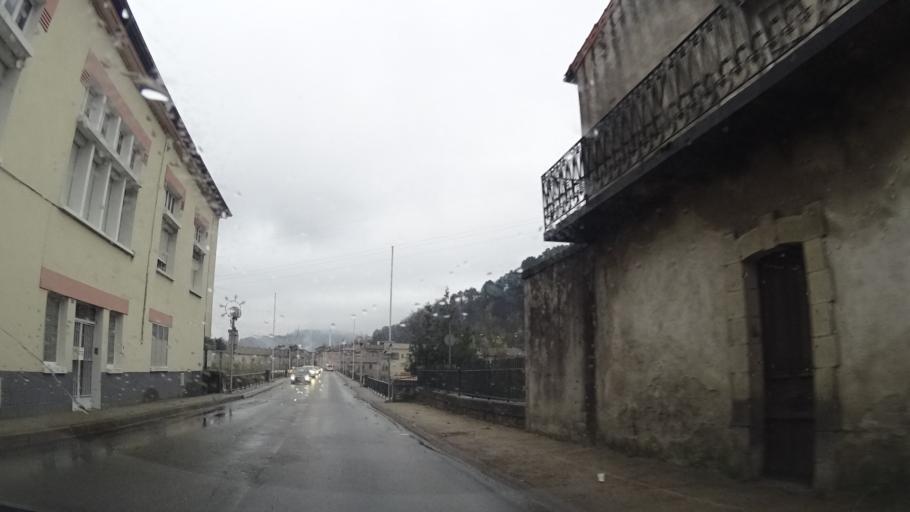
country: FR
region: Rhone-Alpes
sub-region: Departement de l'Ardeche
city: Labegude
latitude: 44.6524
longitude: 4.3650
